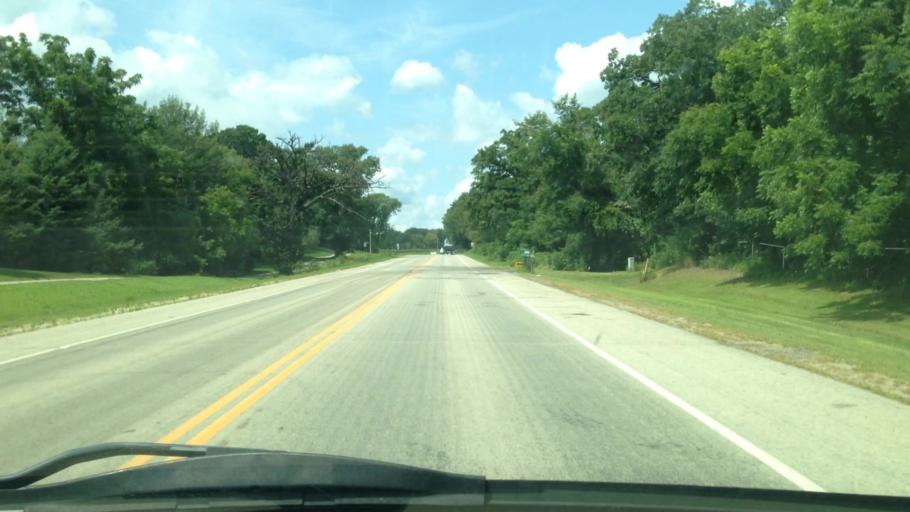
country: US
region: Minnesota
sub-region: Olmsted County
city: Rochester
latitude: 43.9531
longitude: -92.4946
